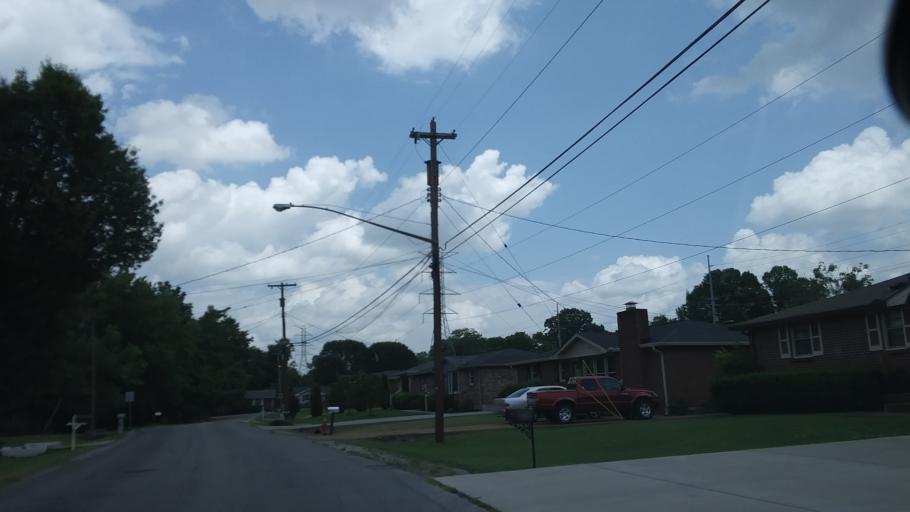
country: US
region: Tennessee
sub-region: Davidson County
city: Belle Meade
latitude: 36.1491
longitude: -86.8869
